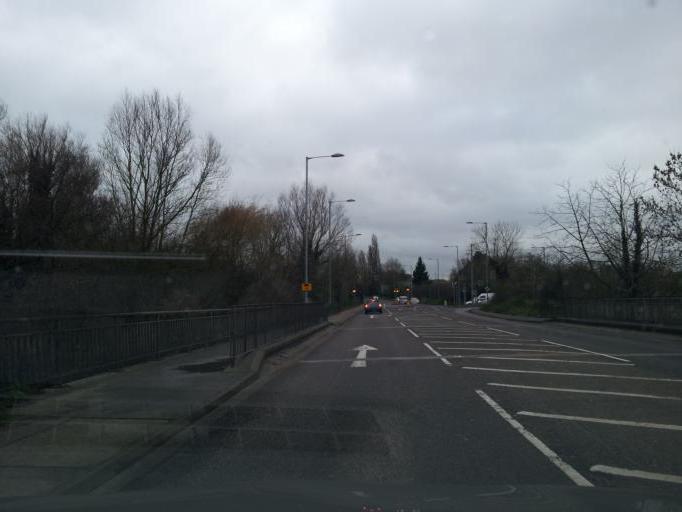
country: GB
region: England
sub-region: Norfolk
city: Cringleford
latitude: 52.5980
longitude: 1.2768
